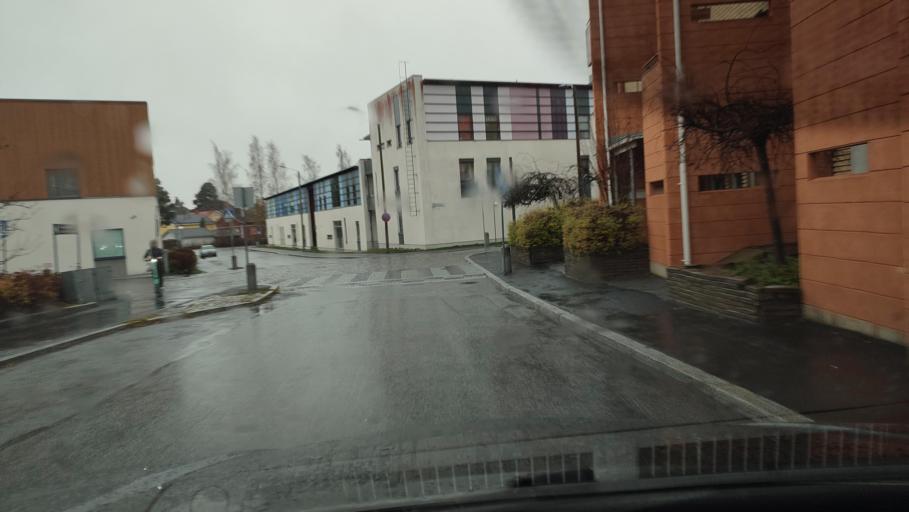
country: FI
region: Ostrobothnia
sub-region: Vaasa
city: Vaasa
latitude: 63.0916
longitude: 21.6358
